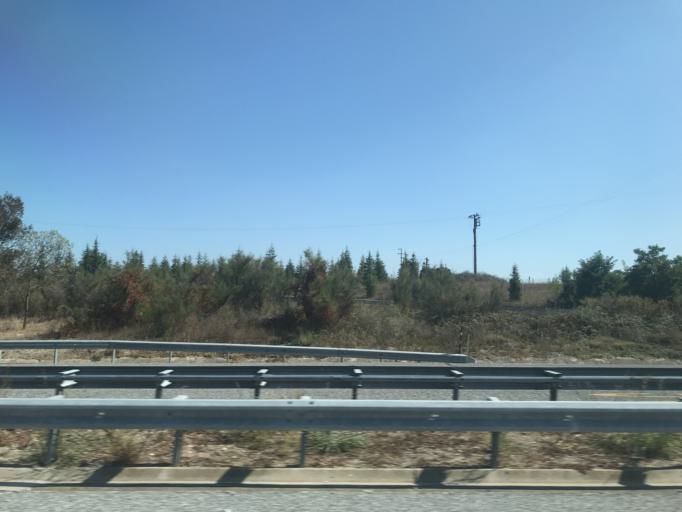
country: TR
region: Kirklareli
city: Luleburgaz
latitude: 41.4393
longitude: 27.3863
